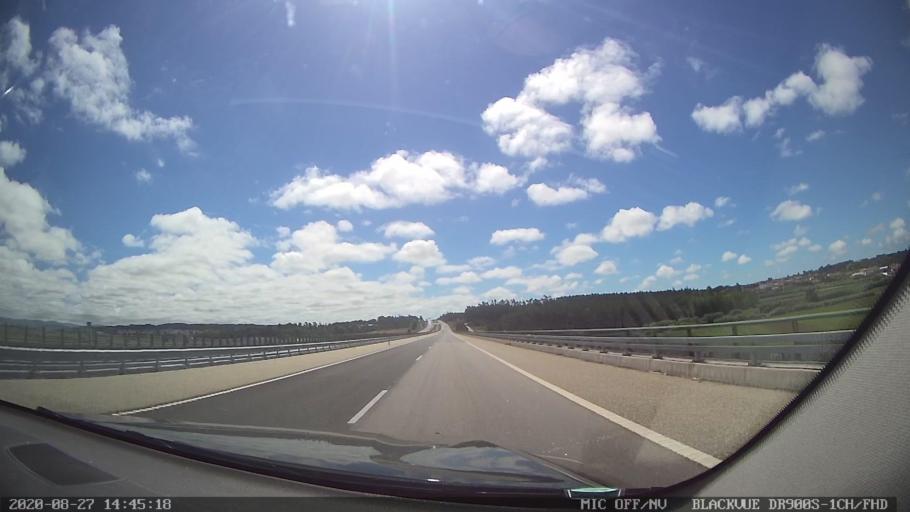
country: PT
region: Leiria
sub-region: Leiria
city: Amor
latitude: 39.8071
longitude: -8.8476
